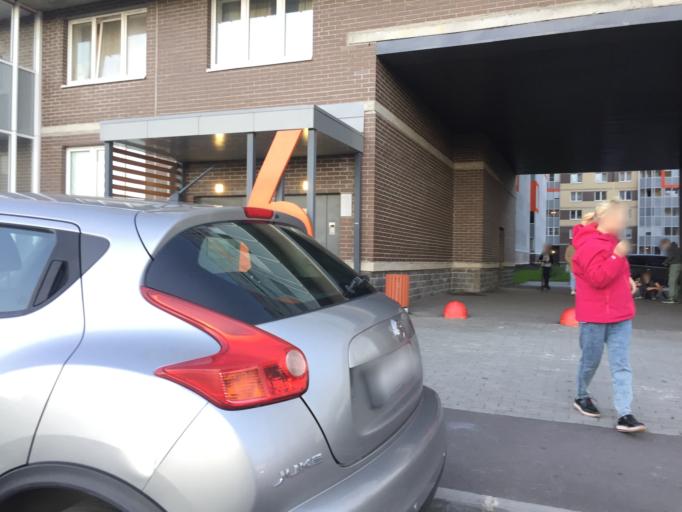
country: RU
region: St.-Petersburg
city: Grazhdanka
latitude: 60.0551
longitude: 30.4144
